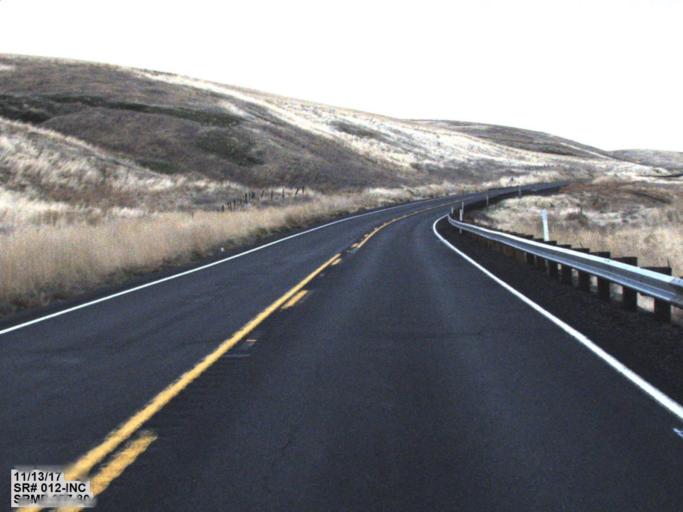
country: US
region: Washington
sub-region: Columbia County
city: Dayton
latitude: 46.4498
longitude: -117.9582
